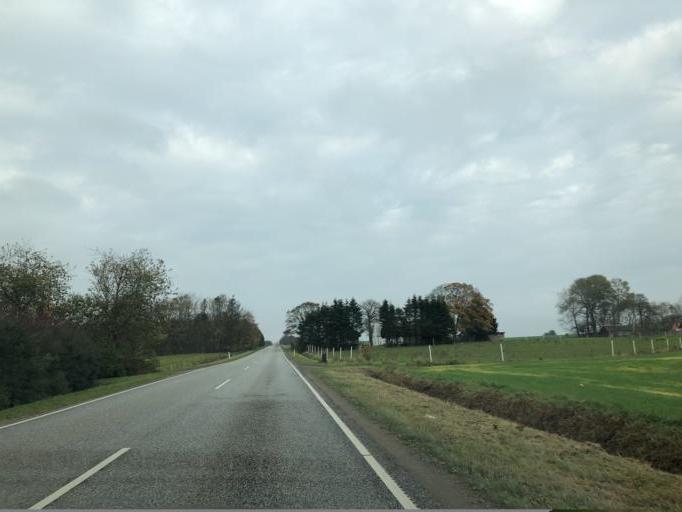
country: DK
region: Central Jutland
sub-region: Hedensted Kommune
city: Hornsyld
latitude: 55.7364
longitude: 9.8123
